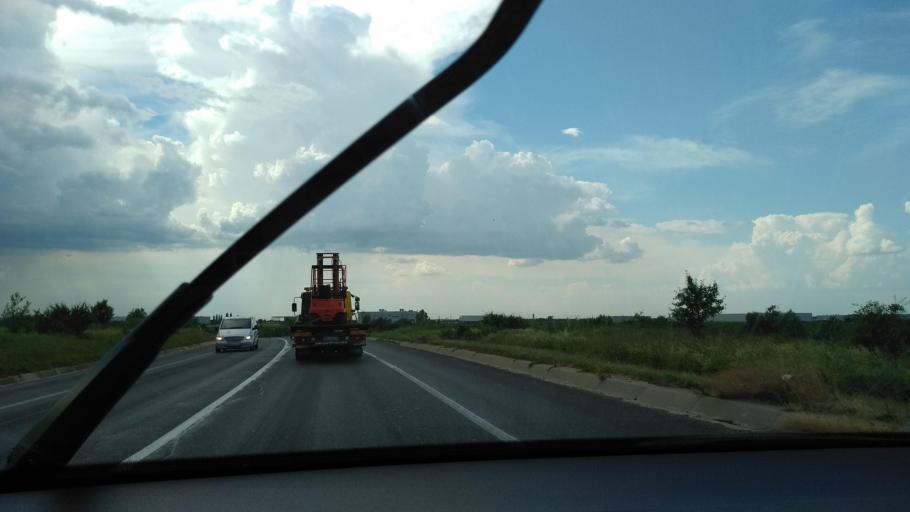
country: RO
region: Timis
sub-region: Comuna Ghiroda
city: Giarmata-Vii
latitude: 45.8123
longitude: 21.2905
